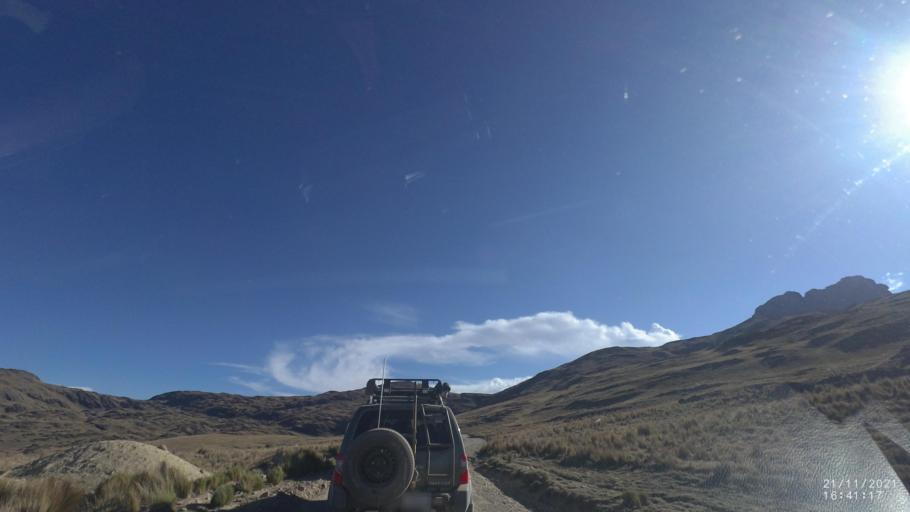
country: BO
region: Cochabamba
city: Cochabamba
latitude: -17.0649
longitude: -66.2561
